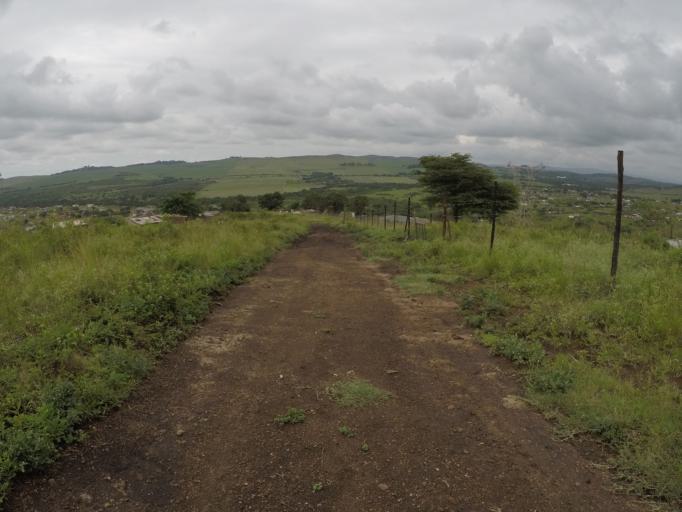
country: ZA
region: KwaZulu-Natal
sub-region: uThungulu District Municipality
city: Empangeni
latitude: -28.7073
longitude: 31.8516
